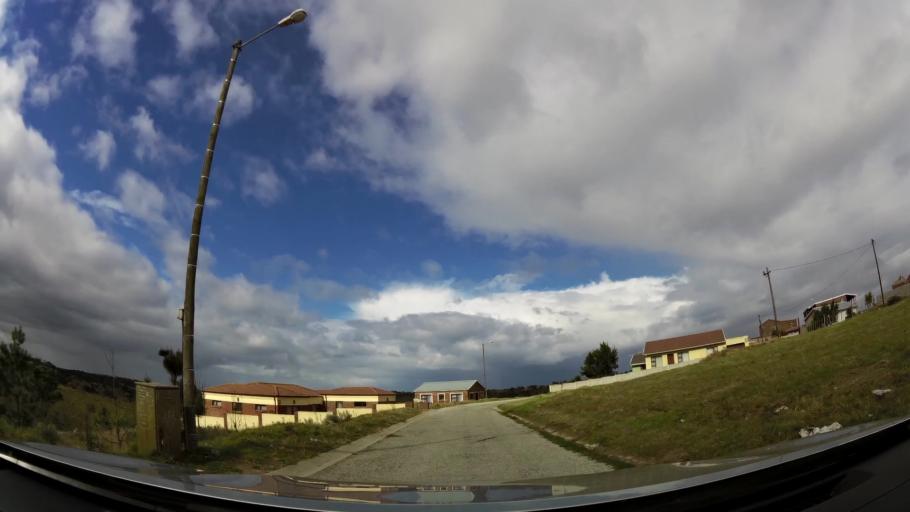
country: ZA
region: Western Cape
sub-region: Eden District Municipality
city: George
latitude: -34.0260
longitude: 22.4767
